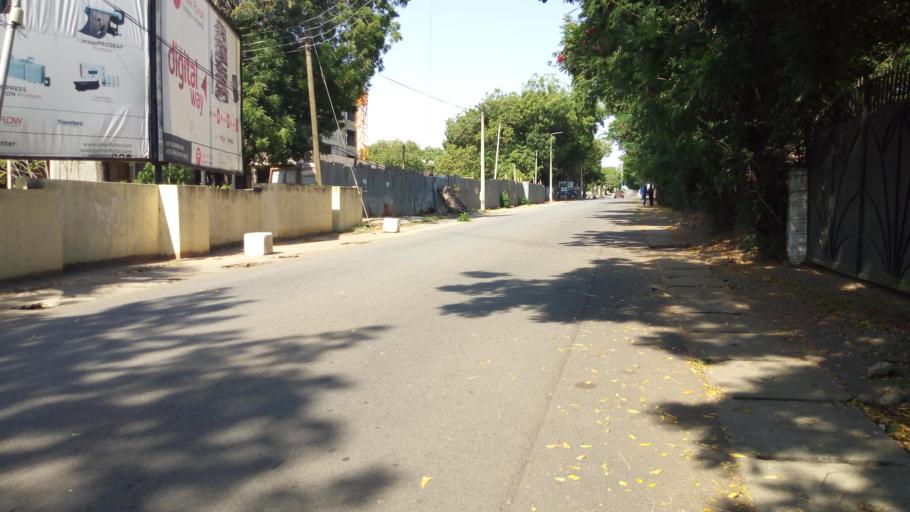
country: GH
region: Greater Accra
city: Accra
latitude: 5.5570
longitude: -0.1972
